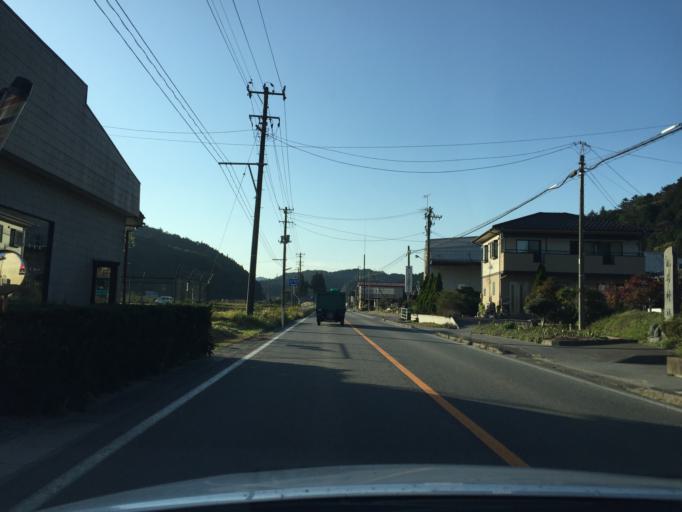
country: JP
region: Fukushima
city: Iwaki
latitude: 37.1202
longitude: 140.7425
